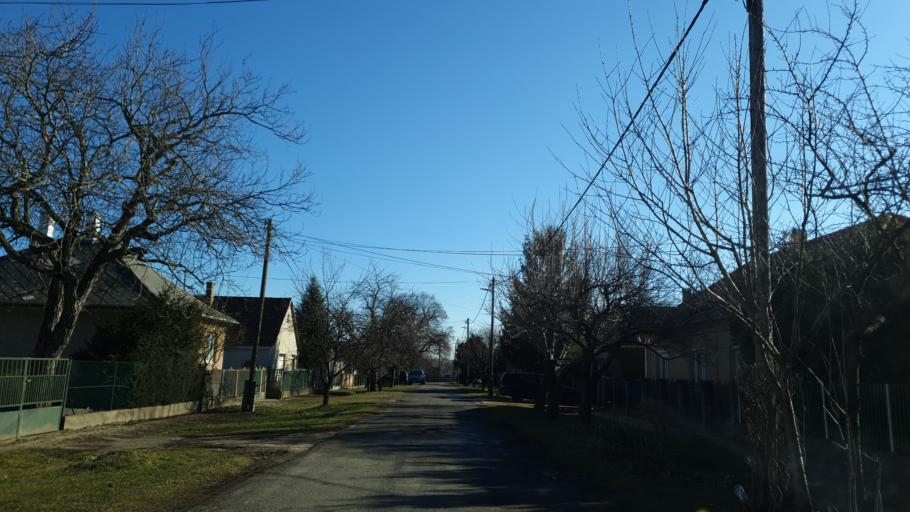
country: HU
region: Fejer
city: Csakvar
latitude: 47.3959
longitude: 18.4731
